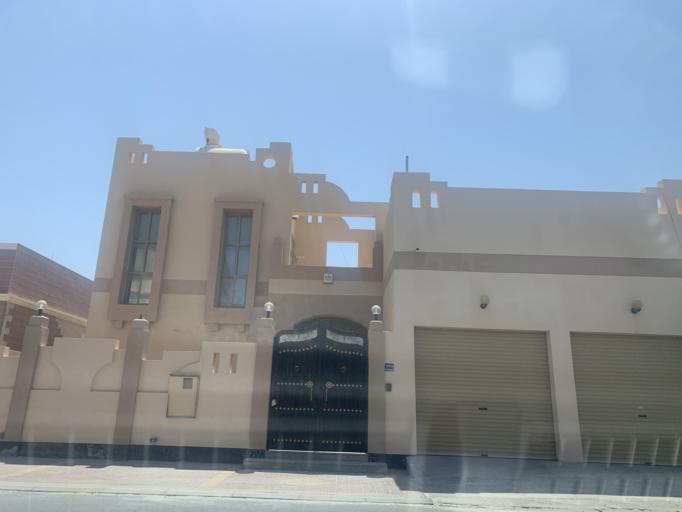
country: BH
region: Muharraq
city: Al Muharraq
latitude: 26.2870
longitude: 50.6215
